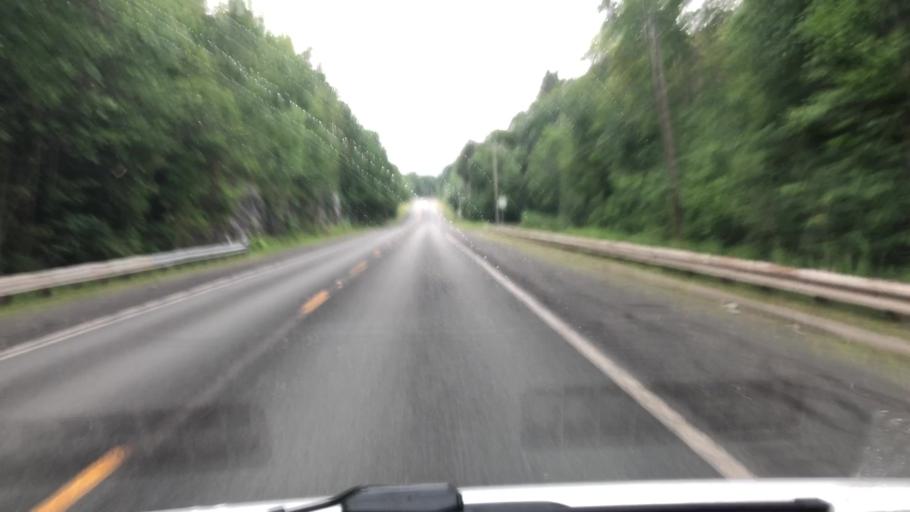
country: US
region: Massachusetts
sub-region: Berkshire County
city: Lanesborough
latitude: 42.6006
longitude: -73.2408
